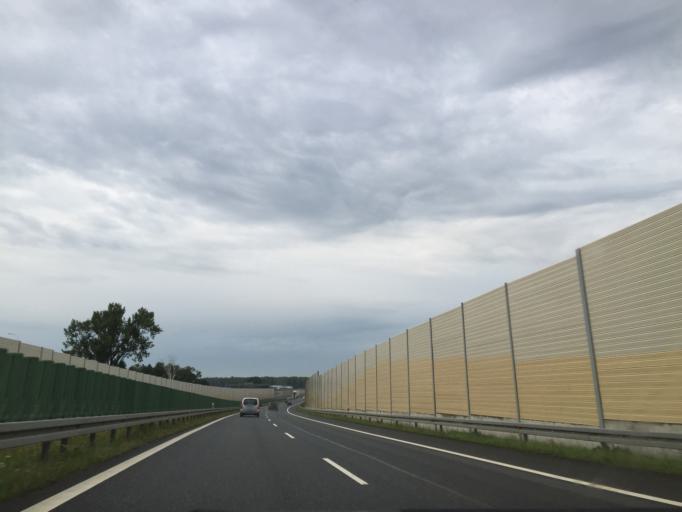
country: PL
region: Podlasie
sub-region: Powiat zambrowski
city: Zambrow
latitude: 52.9885
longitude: 22.2203
